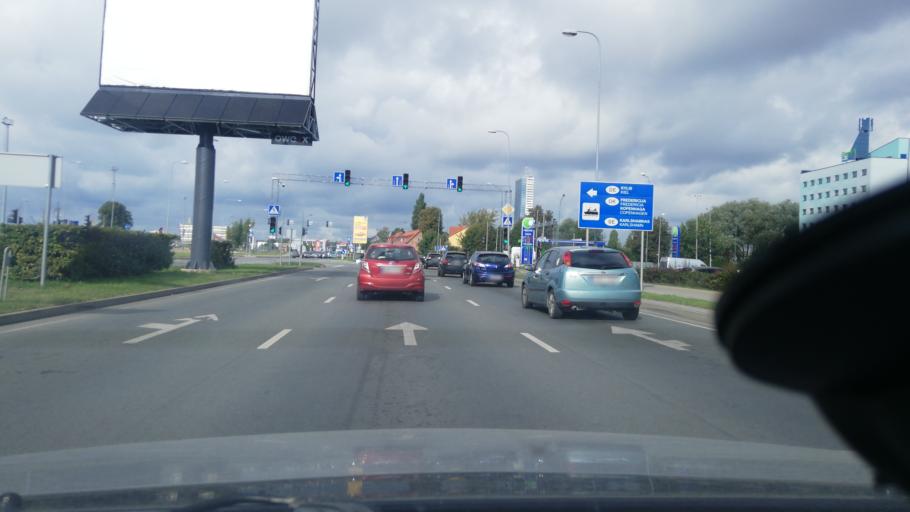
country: LT
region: Klaipedos apskritis
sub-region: Klaipeda
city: Klaipeda
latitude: 55.6831
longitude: 21.1500
